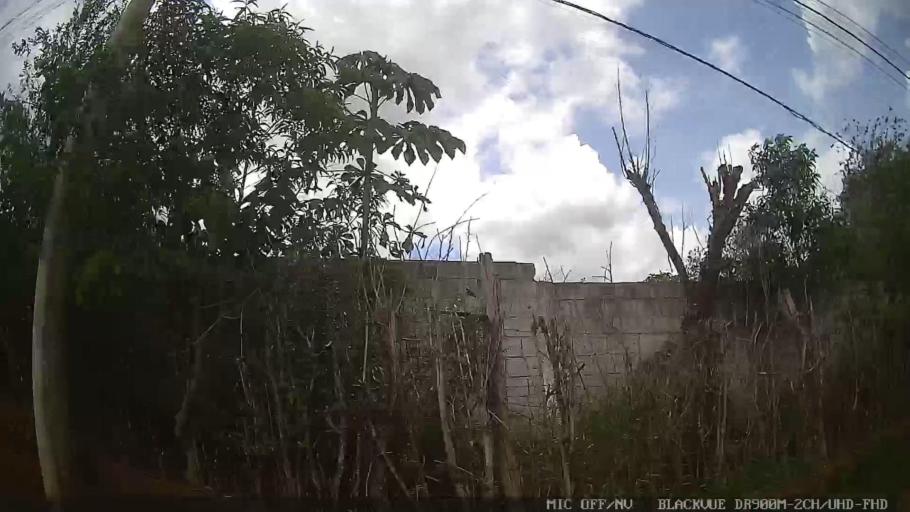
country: BR
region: Sao Paulo
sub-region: Suzano
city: Suzano
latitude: -23.6081
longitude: -46.2394
